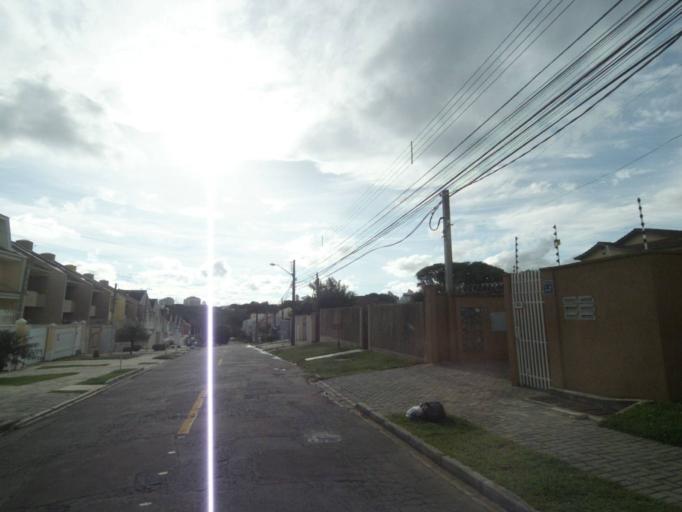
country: BR
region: Parana
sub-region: Curitiba
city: Curitiba
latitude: -25.4415
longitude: -49.3098
